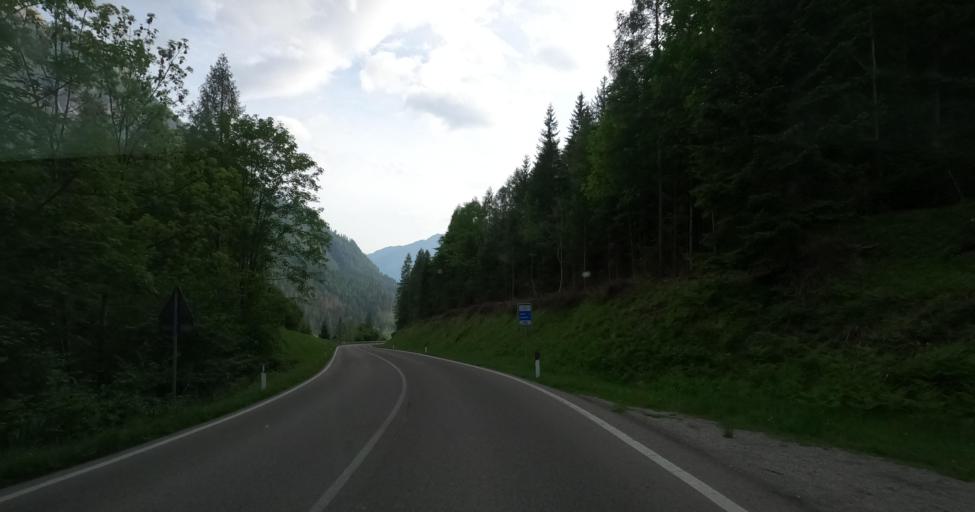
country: IT
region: Veneto
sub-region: Provincia di Belluno
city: Celat-San Tomaso Agordino
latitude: 46.3913
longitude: 11.9985
